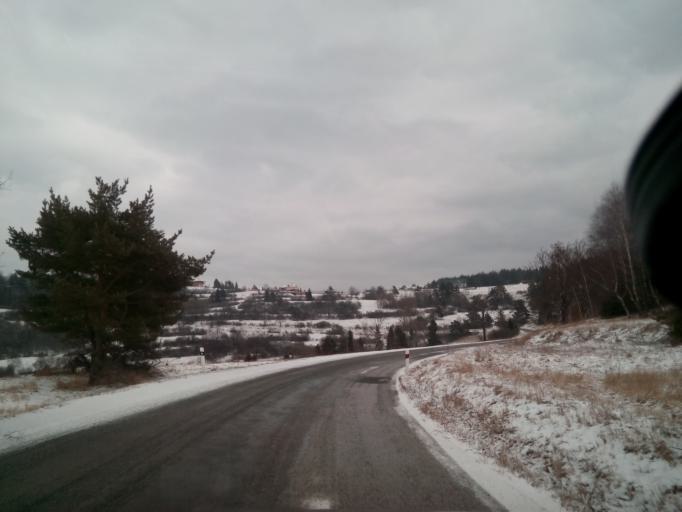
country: SK
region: Presovsky
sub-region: Okres Presov
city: Levoca
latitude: 49.0381
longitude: 20.6361
